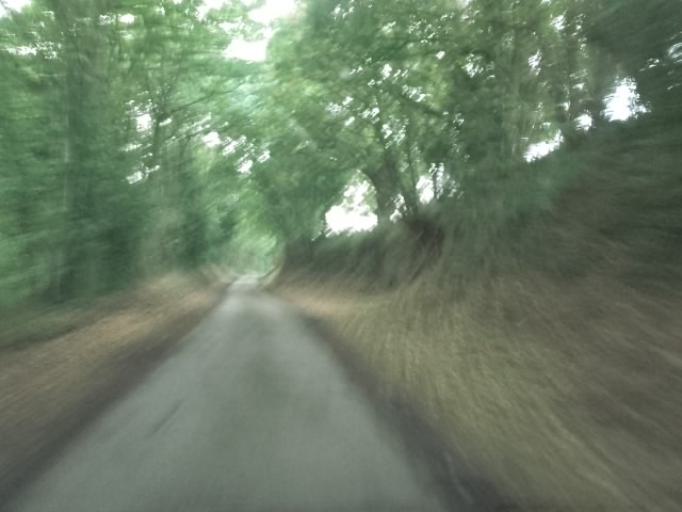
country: FR
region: Brittany
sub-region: Departement des Cotes-d'Armor
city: Pleguien
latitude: 48.6371
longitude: -2.9476
